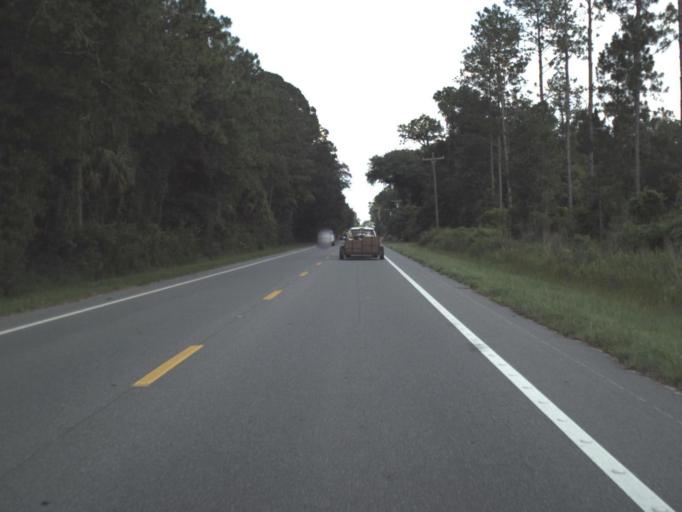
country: US
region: Florida
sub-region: Putnam County
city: Palatka
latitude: 29.6828
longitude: -81.7304
